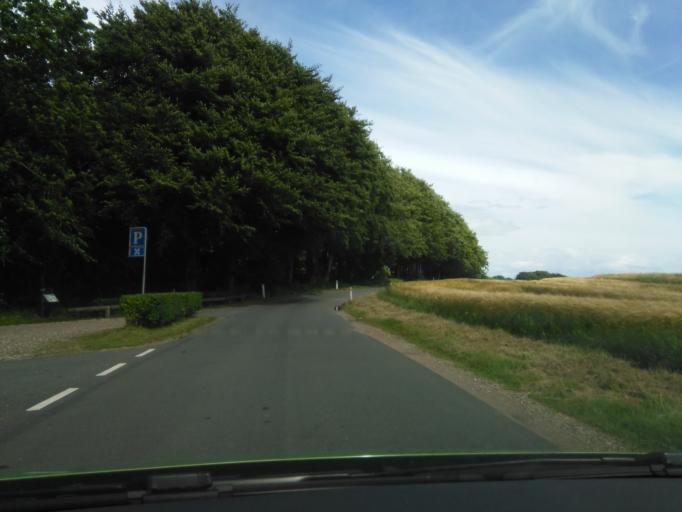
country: DK
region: Central Jutland
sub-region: Skanderborg Kommune
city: Ry
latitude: 55.9919
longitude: 9.7946
